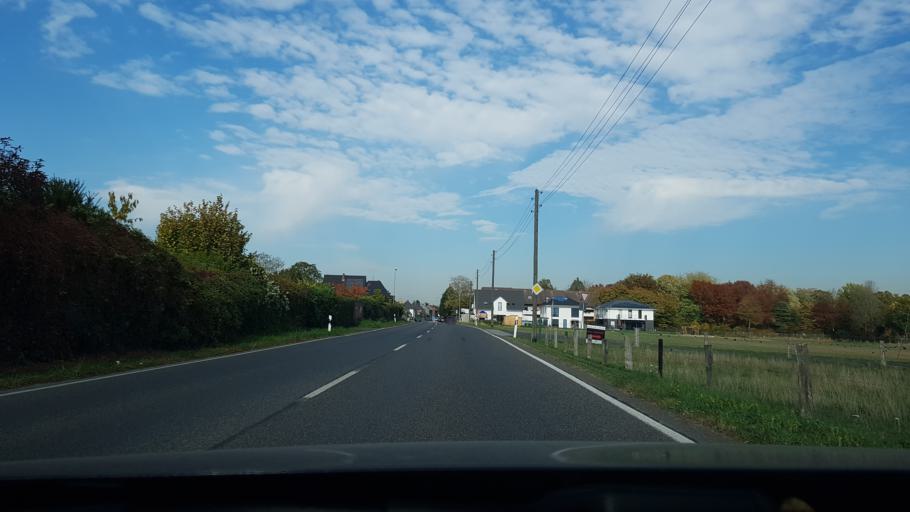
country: DE
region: North Rhine-Westphalia
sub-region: Regierungsbezirk Dusseldorf
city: Moers
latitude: 51.4367
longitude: 6.5753
